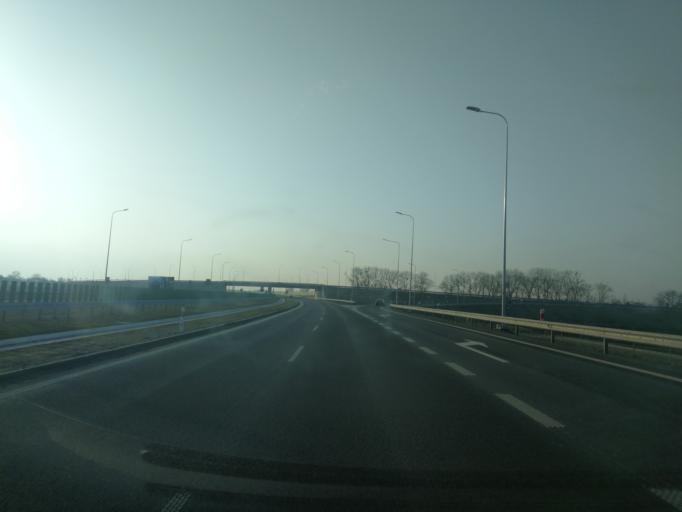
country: PL
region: Warmian-Masurian Voivodeship
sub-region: Powiat elblaski
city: Elblag
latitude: 54.1634
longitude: 19.3500
